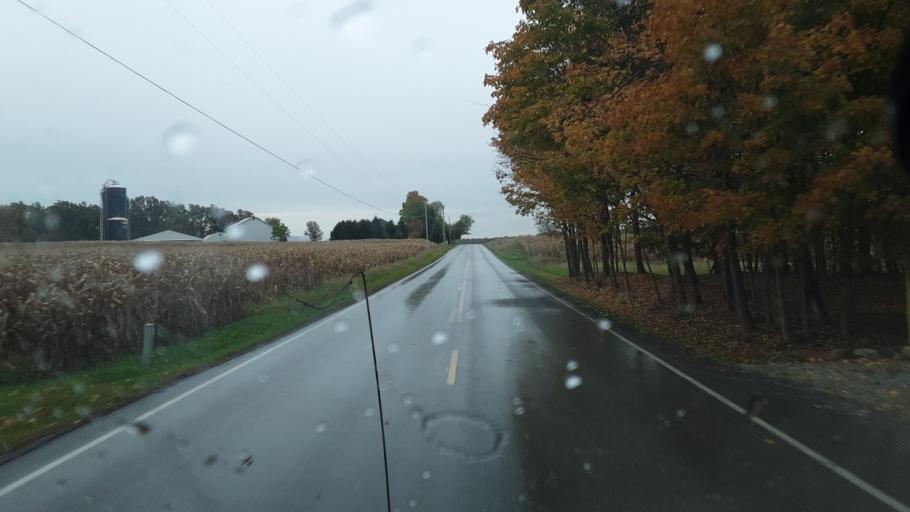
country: US
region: Ohio
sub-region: Wayne County
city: West Salem
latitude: 40.9301
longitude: -82.0725
